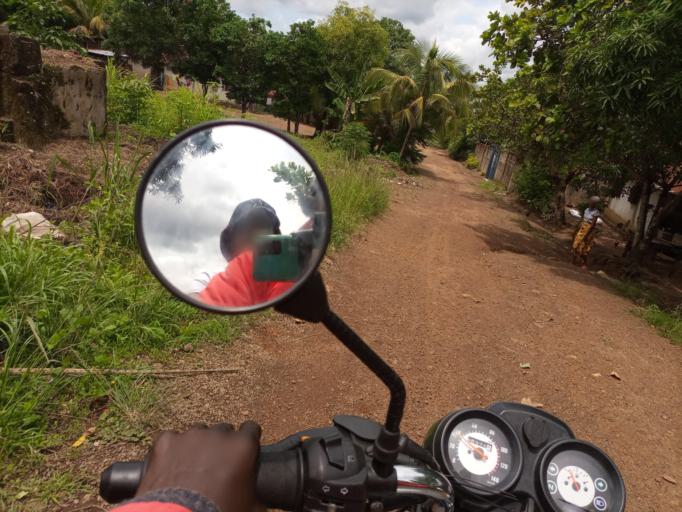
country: SL
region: Southern Province
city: Baoma
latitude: 7.9700
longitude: -11.7136
